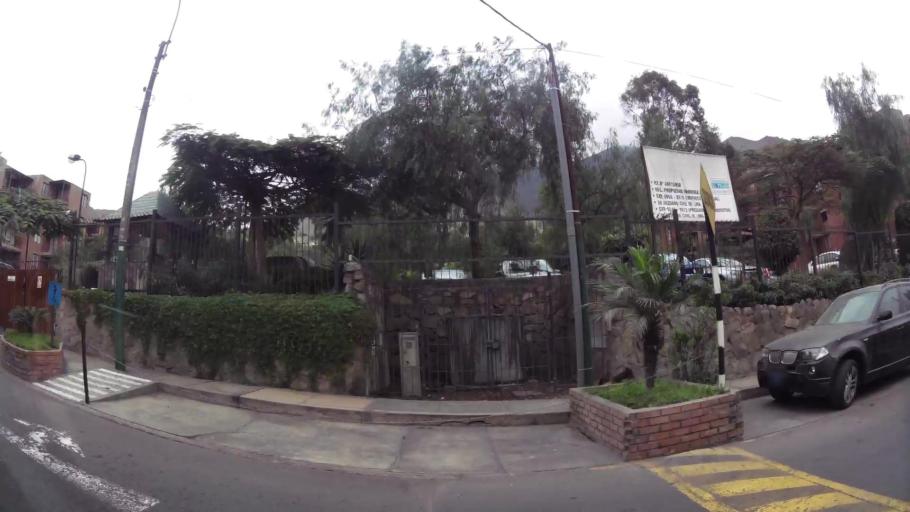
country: PE
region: Lima
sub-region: Lima
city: La Molina
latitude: -12.1071
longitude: -76.9583
